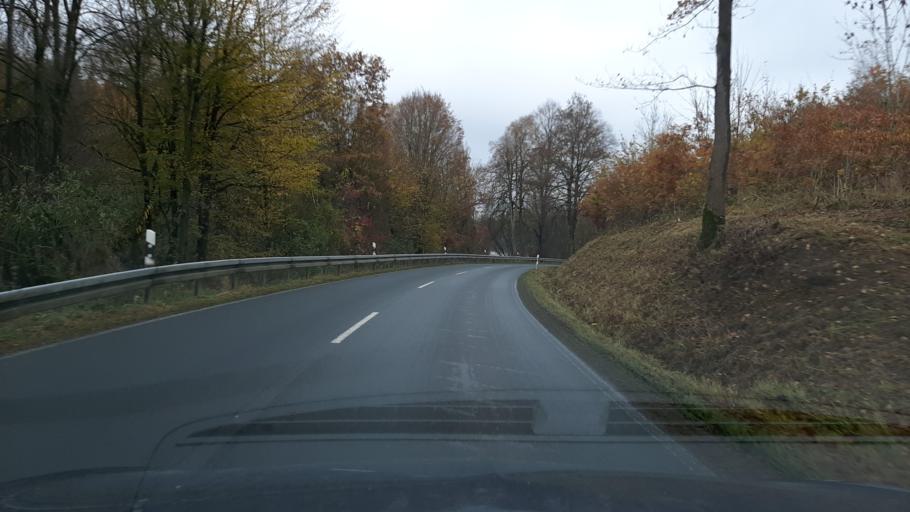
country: DE
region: North Rhine-Westphalia
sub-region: Regierungsbezirk Arnsberg
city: Olsberg
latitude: 51.2666
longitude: 8.4751
